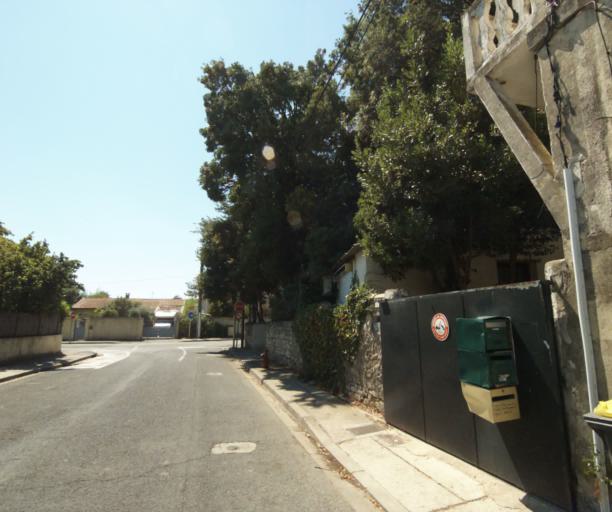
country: FR
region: Languedoc-Roussillon
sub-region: Departement de l'Herault
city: Marsillargues
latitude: 43.6667
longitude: 4.1742
